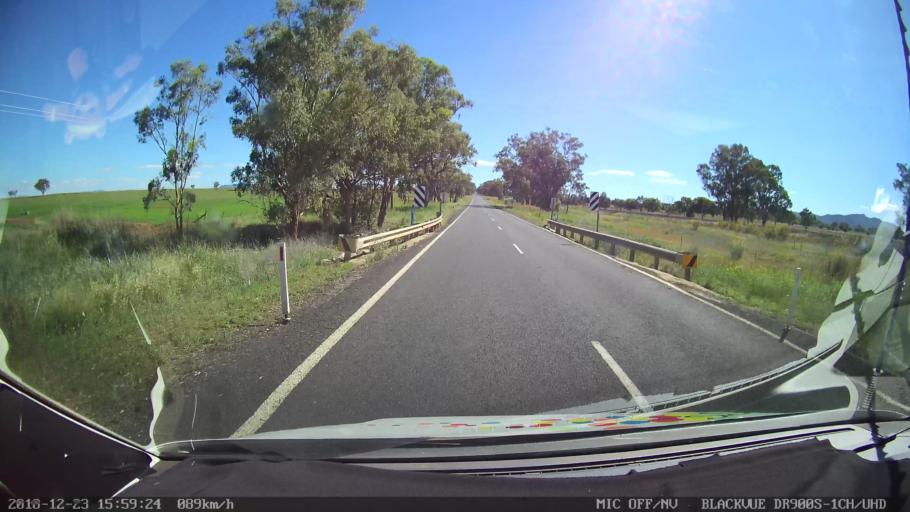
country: AU
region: New South Wales
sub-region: Tamworth Municipality
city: Phillip
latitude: -31.1994
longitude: 150.8335
